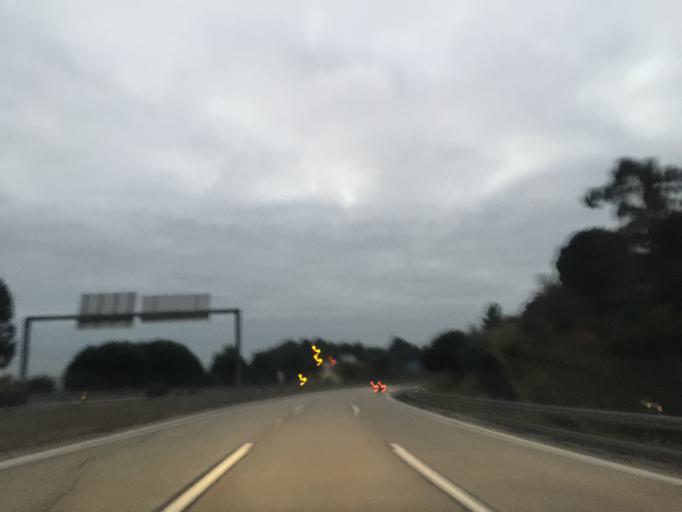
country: PT
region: Lisbon
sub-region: Vila Franca de Xira
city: Sobralinho
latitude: 38.9053
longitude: -9.0597
